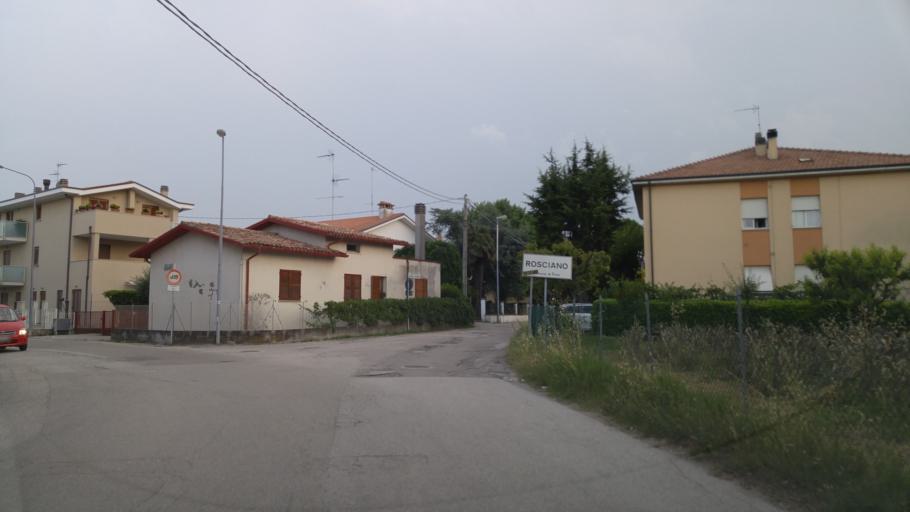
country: IT
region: The Marches
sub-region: Provincia di Pesaro e Urbino
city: Rosciano
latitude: 43.8218
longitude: 12.9962
